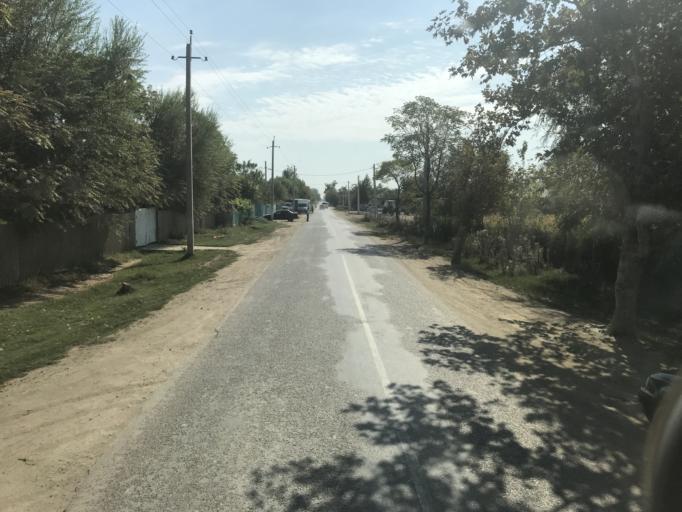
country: KZ
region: Ongtustik Qazaqstan
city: Myrzakent
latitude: 40.6643
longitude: 68.6182
